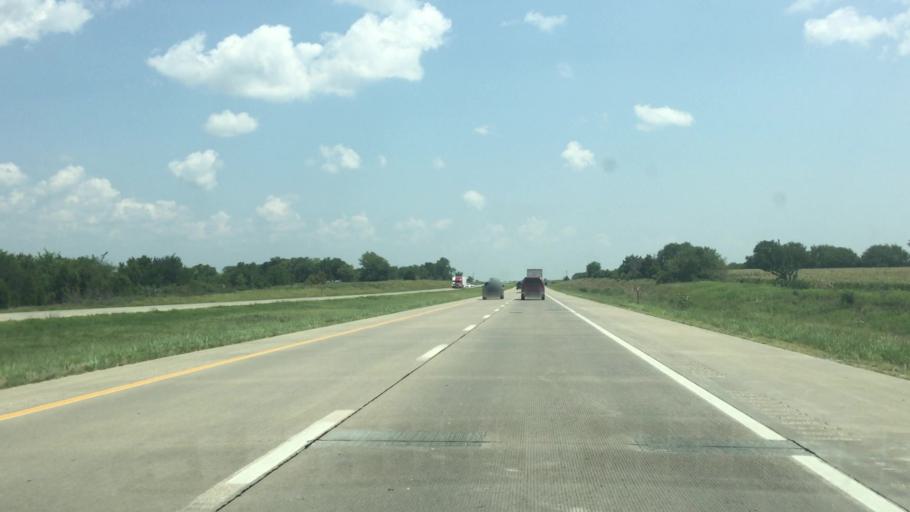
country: US
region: Kansas
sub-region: Franklin County
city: Wellsville
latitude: 38.7250
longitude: -95.0364
